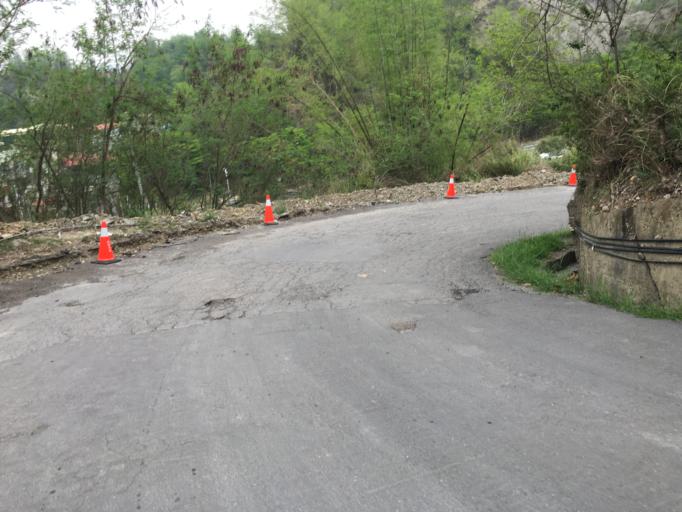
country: TW
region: Taiwan
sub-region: Tainan
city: Tainan
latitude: 22.8865
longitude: 120.3899
